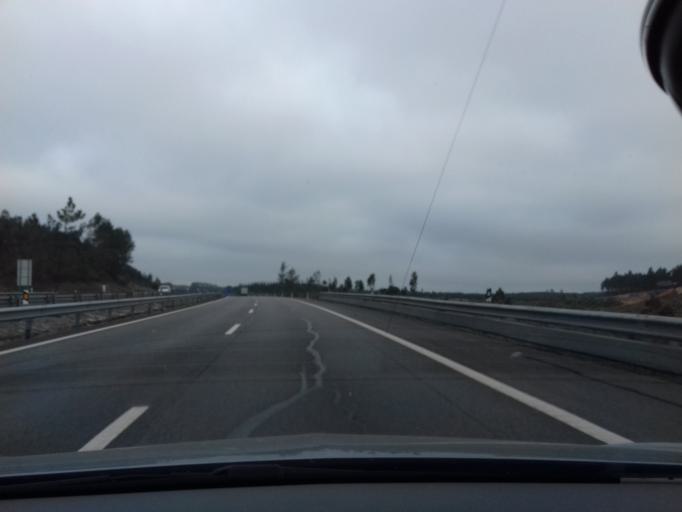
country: PT
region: Lisbon
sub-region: Torres Vedras
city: A dos Cunhados
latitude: 39.1800
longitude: -9.2040
